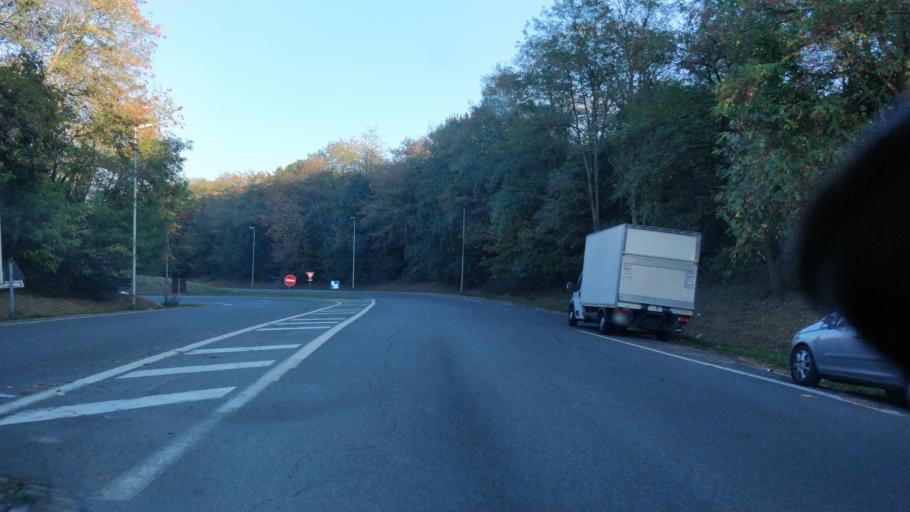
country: FR
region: Ile-de-France
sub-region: Departement de Seine-Saint-Denis
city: Gournay-sur-Marne
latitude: 48.8487
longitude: 2.5860
